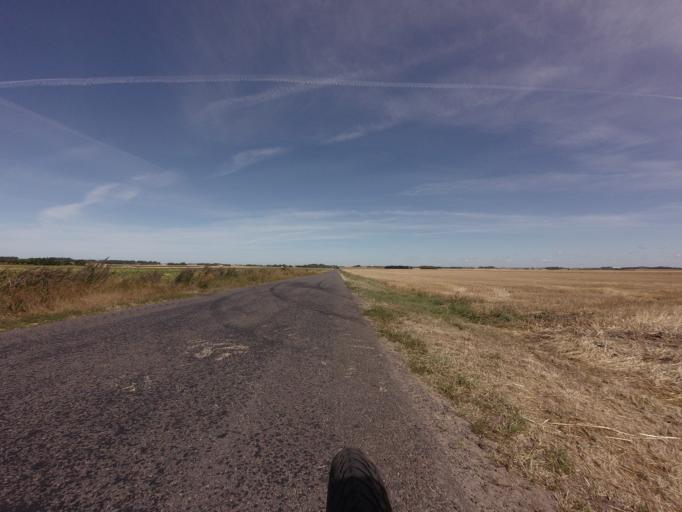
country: DK
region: North Denmark
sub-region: Bronderslev Kommune
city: Bronderslev
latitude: 57.3095
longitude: 9.8097
